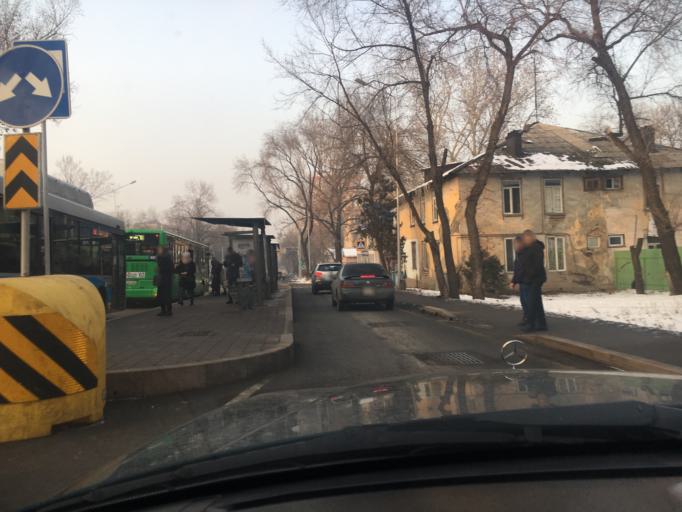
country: KZ
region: Almaty Qalasy
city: Almaty
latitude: 43.2092
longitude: 76.8788
